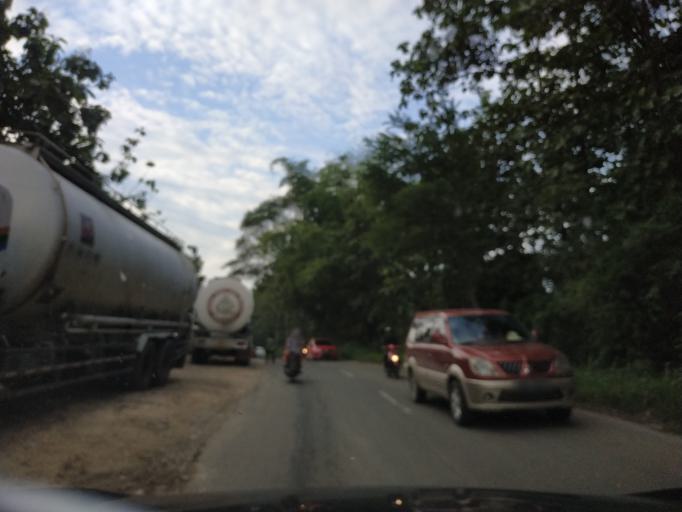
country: ID
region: Central Java
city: Ngampel
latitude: -6.8979
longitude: 111.4402
